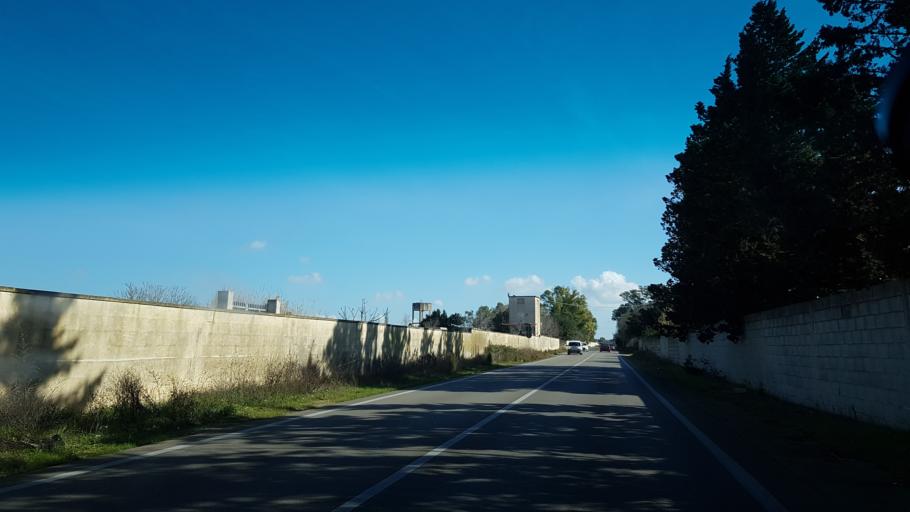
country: IT
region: Apulia
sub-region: Provincia di Lecce
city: Arnesano
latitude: 40.3595
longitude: 18.1092
